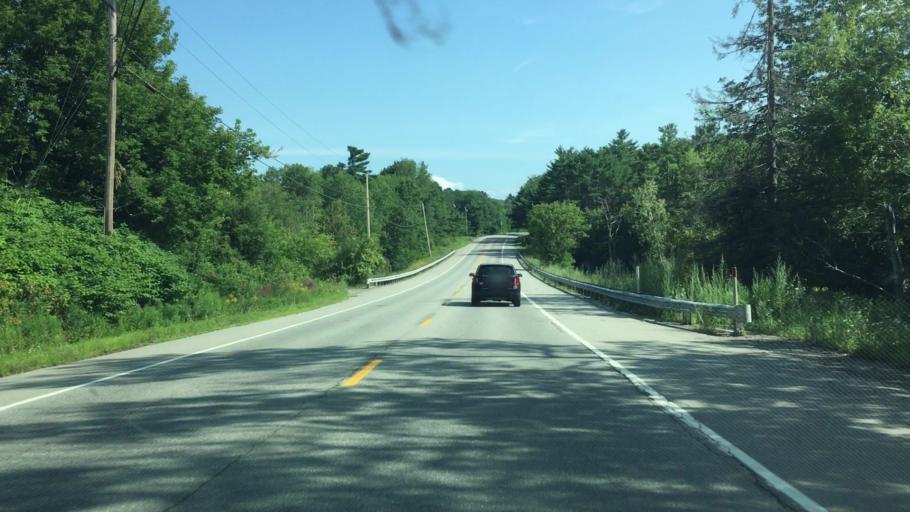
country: US
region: Maine
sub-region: Waldo County
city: Winterport
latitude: 44.6694
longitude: -68.8342
